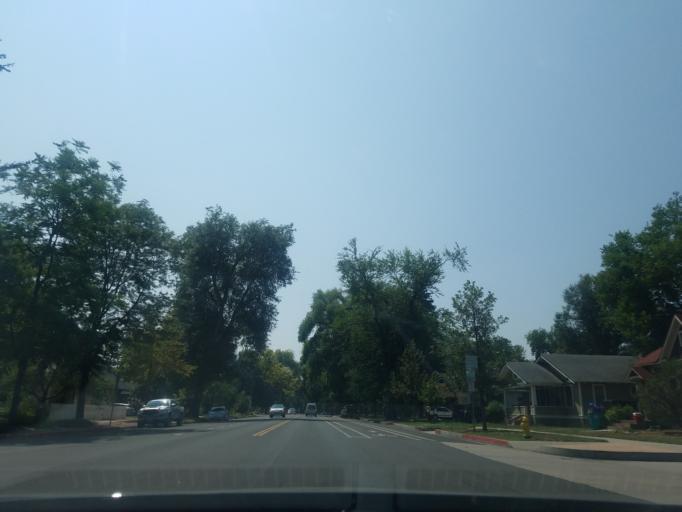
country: US
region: Colorado
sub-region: Larimer County
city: Fort Collins
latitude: 40.5722
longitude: -105.0756
